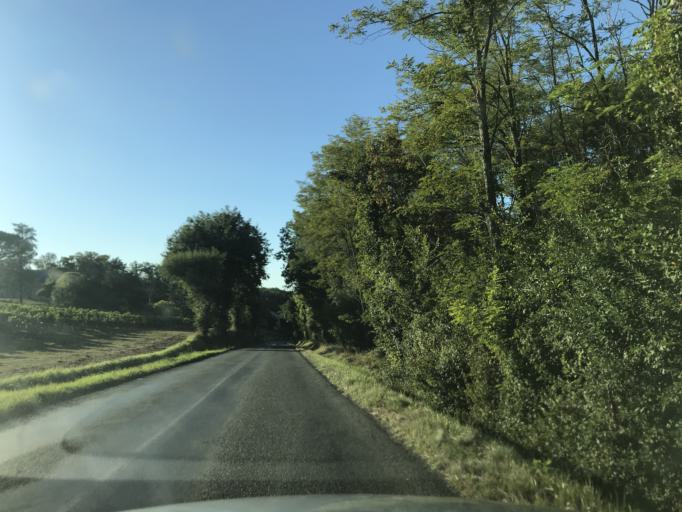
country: FR
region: Aquitaine
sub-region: Departement de la Gironde
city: Mouliets-et-Villemartin
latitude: 44.7870
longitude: -0.0472
